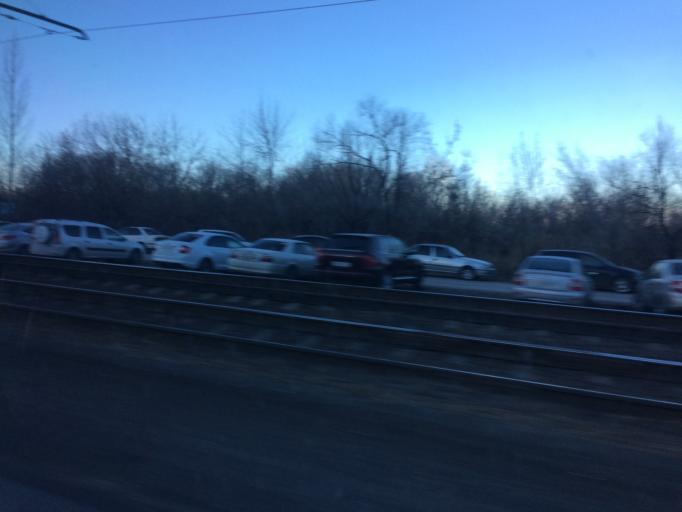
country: RU
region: Chelyabinsk
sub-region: Gorod Magnitogorsk
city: Magnitogorsk
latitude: 53.4011
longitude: 59.0254
